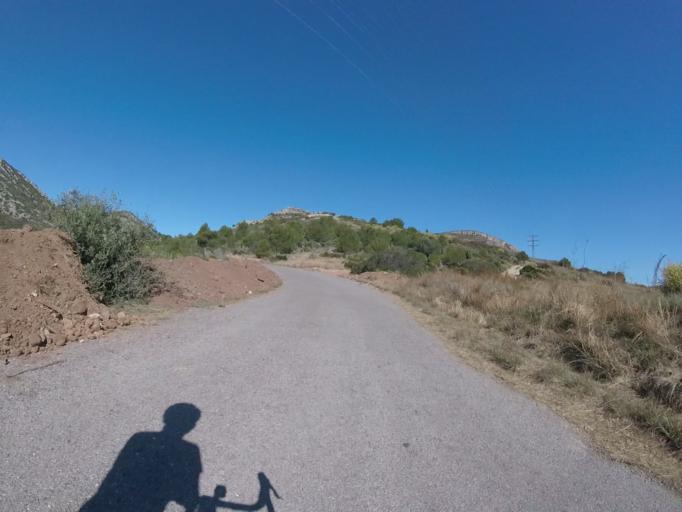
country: ES
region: Valencia
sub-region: Provincia de Castello
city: Orpesa/Oropesa del Mar
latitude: 40.0754
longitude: 0.1101
